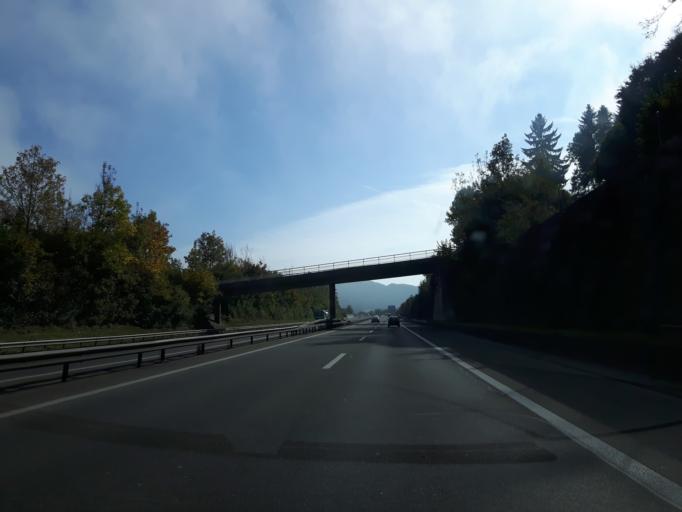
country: CH
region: Lucerne
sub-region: Willisau District
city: Dagmersellen
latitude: 47.2187
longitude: 7.9745
